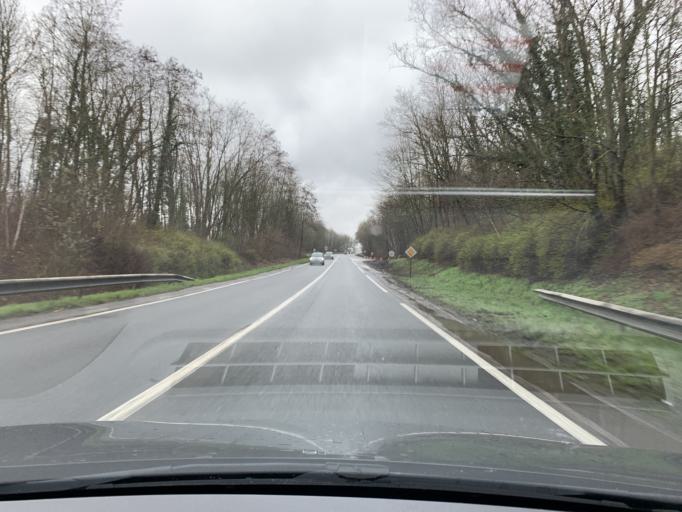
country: FR
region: Nord-Pas-de-Calais
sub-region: Departement du Nord
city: Dechy
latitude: 50.3547
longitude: 3.1223
